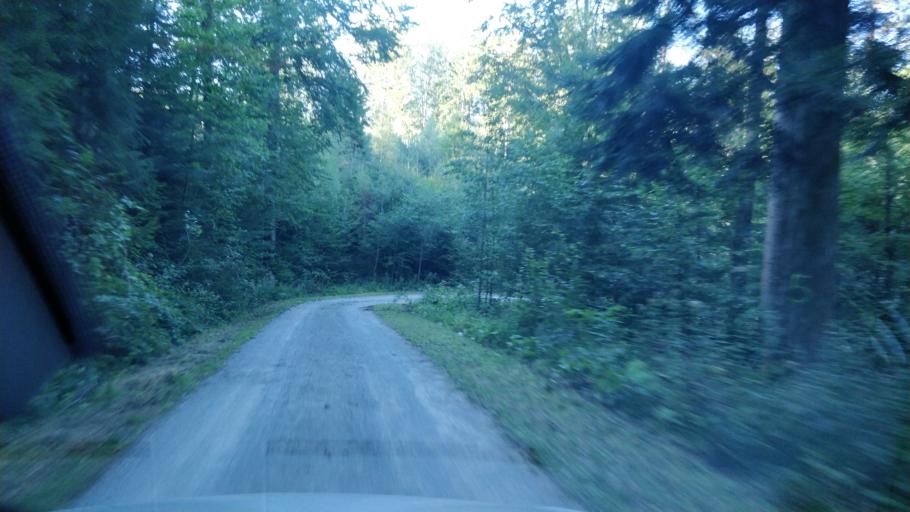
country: DE
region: Baden-Wuerttemberg
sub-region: Regierungsbezirk Stuttgart
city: Murrhardt
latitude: 49.0123
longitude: 9.5724
